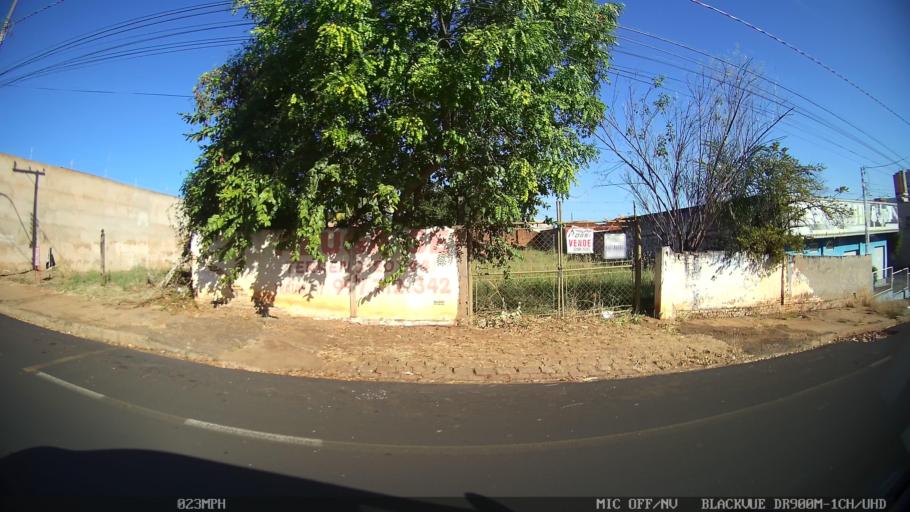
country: BR
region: Sao Paulo
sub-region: Olimpia
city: Olimpia
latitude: -20.7369
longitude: -48.9103
